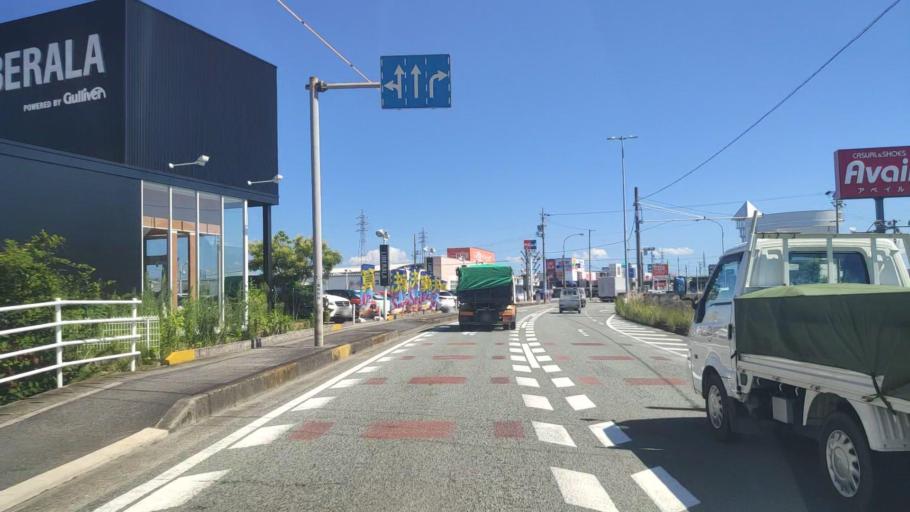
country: JP
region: Mie
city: Tsu-shi
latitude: 34.6863
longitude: 136.5177
